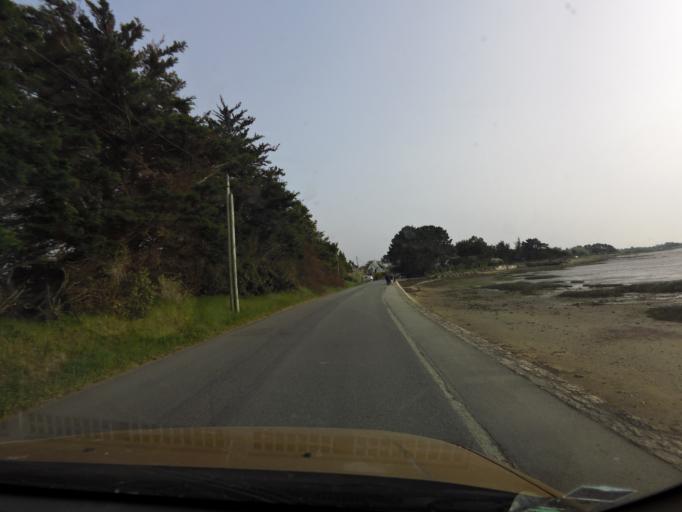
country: FR
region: Brittany
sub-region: Departement du Morbihan
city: Sene
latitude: 47.5807
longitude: -2.7141
